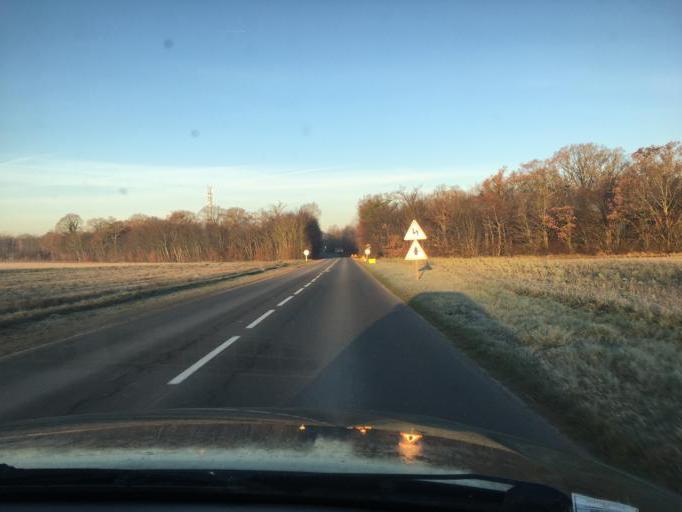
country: FR
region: Centre
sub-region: Departement du Loiret
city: Saran
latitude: 47.9700
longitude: 1.8630
